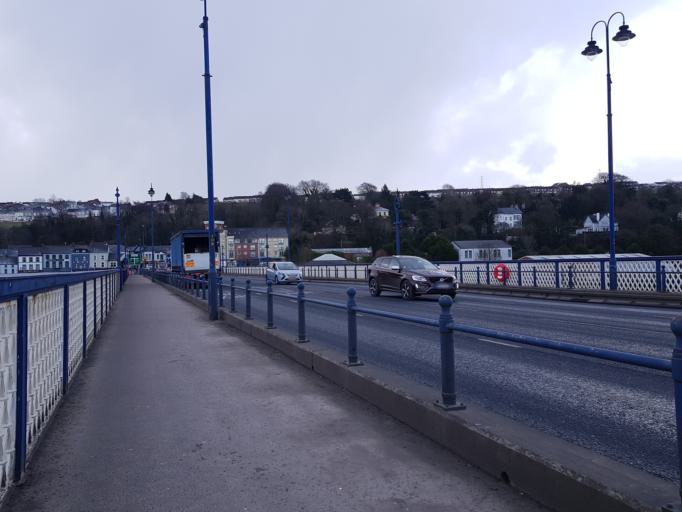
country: GB
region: Northern Ireland
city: Londonderry County Borough
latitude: 54.9907
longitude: -7.3181
